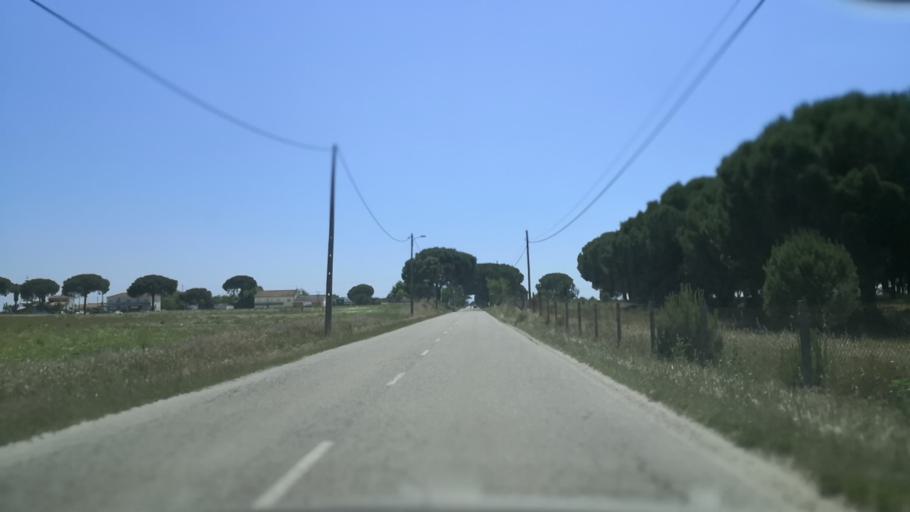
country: PT
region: Santarem
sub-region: Benavente
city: Poceirao
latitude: 38.6902
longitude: -8.7303
